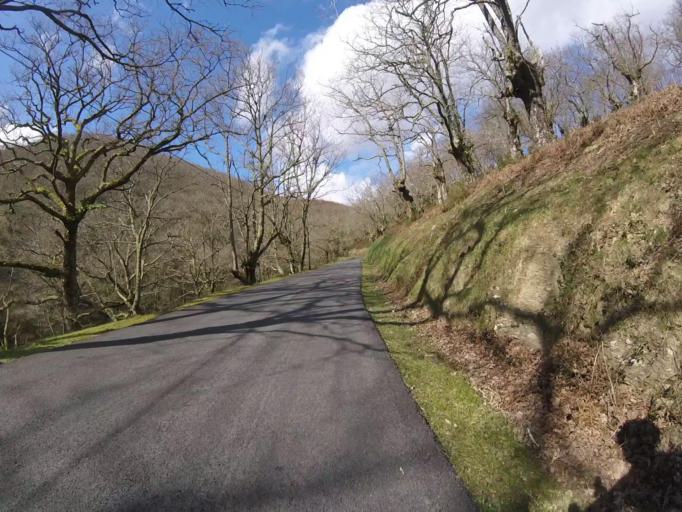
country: ES
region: Navarre
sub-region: Provincia de Navarra
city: Etxalar
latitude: 43.2611
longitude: -1.6135
